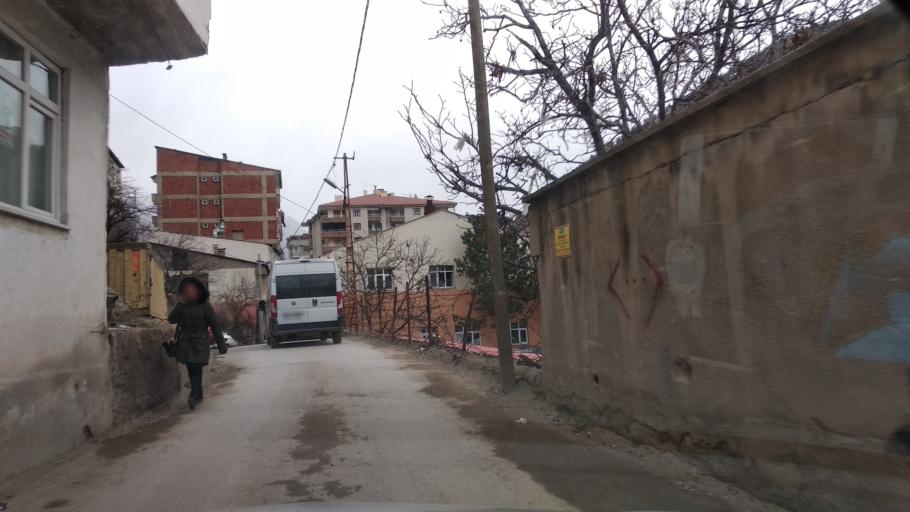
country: TR
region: Gumushane
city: Gumushkhane
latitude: 40.4623
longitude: 39.4683
